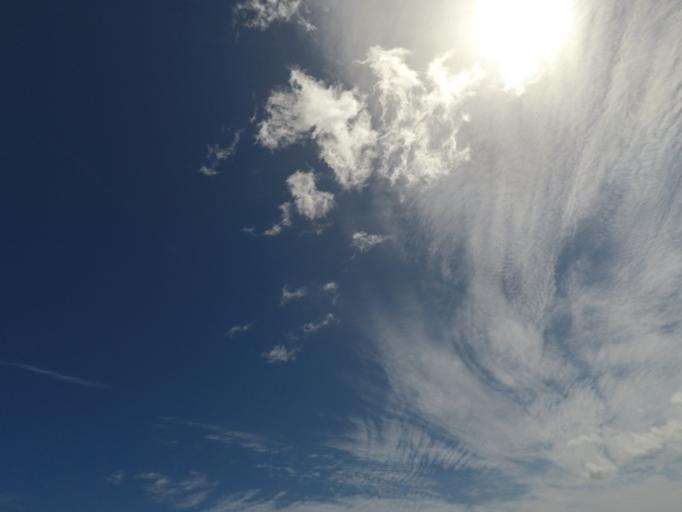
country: PT
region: Madeira
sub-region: Santana
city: Santana
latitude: 32.8257
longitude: -16.9634
